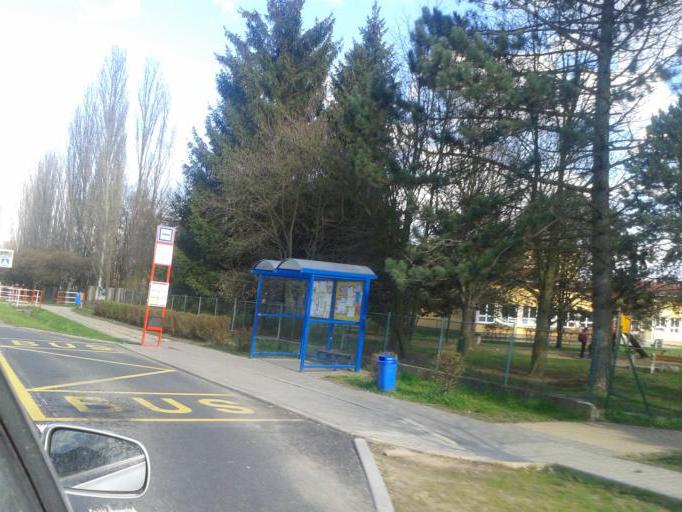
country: CZ
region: Central Bohemia
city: Rudna
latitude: 50.0300
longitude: 14.2213
